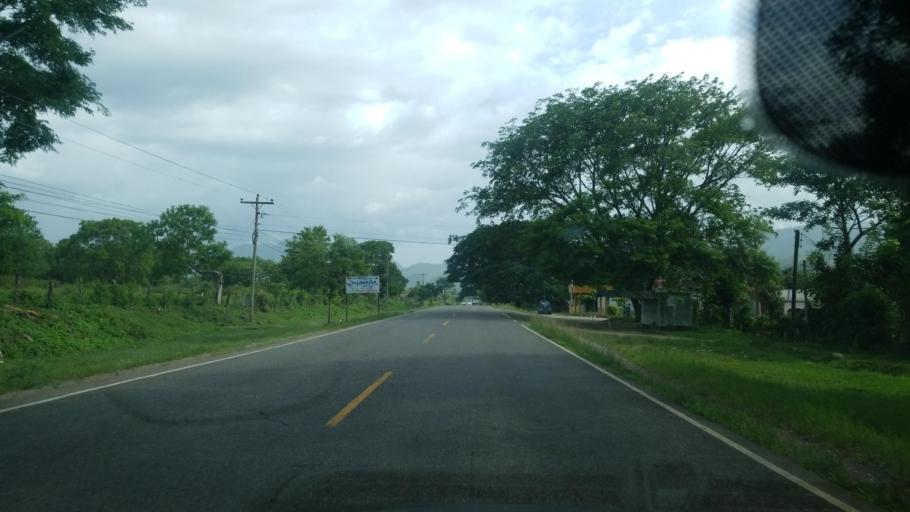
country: HN
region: Ocotepeque
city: Antigua Ocotepeque
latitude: 14.4006
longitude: -89.1970
